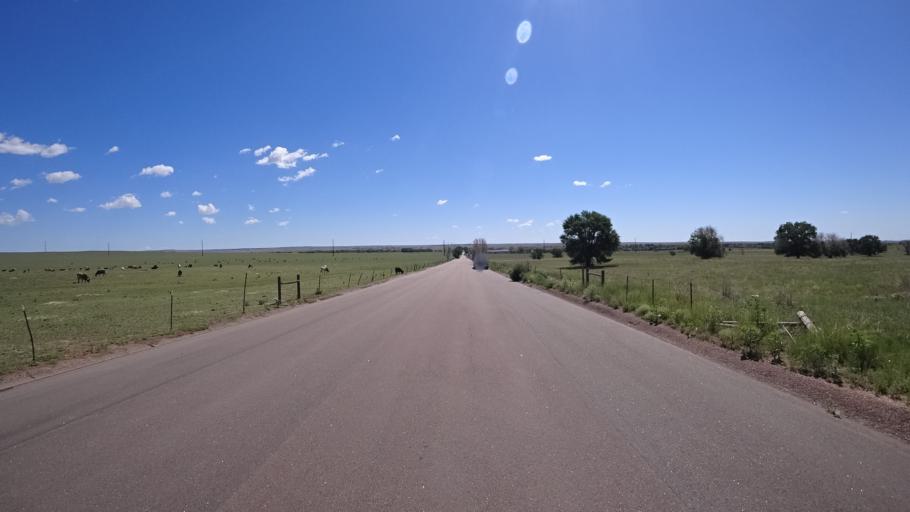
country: US
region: Colorado
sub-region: El Paso County
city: Security-Widefield
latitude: 38.7809
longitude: -104.6733
